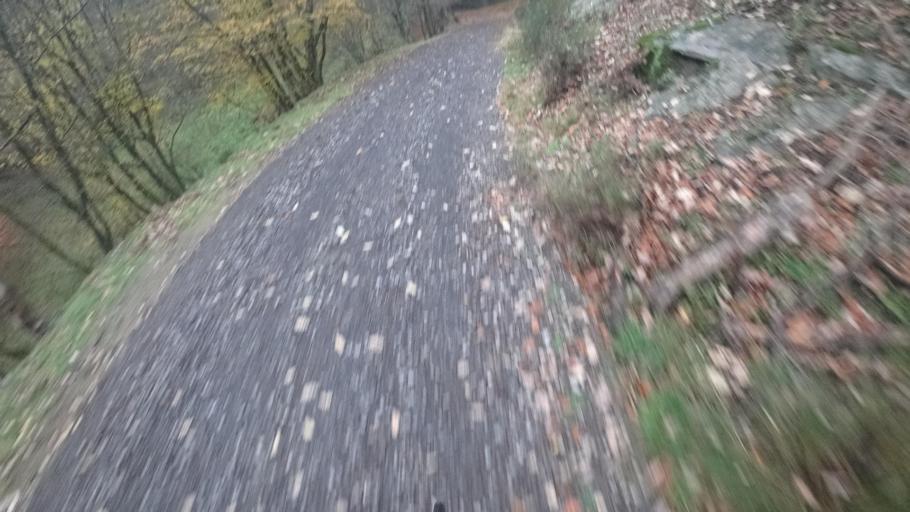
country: DE
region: Rheinland-Pfalz
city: Heckenbach
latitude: 50.4990
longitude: 7.0639
